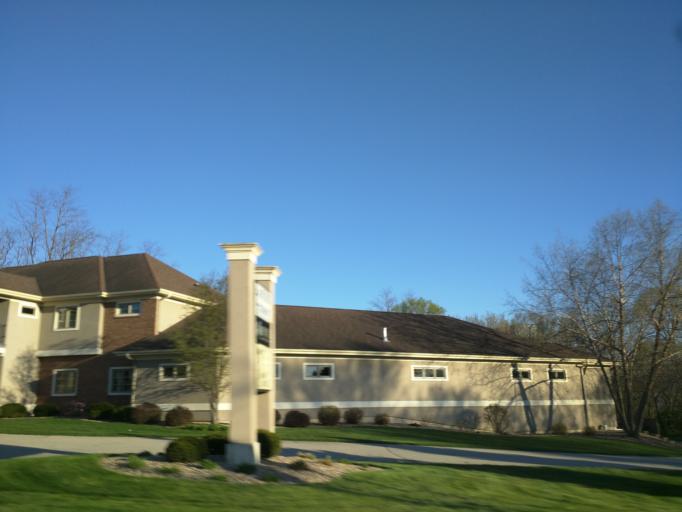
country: US
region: Wisconsin
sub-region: La Crosse County
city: Onalaska
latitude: 43.8673
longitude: -91.2205
